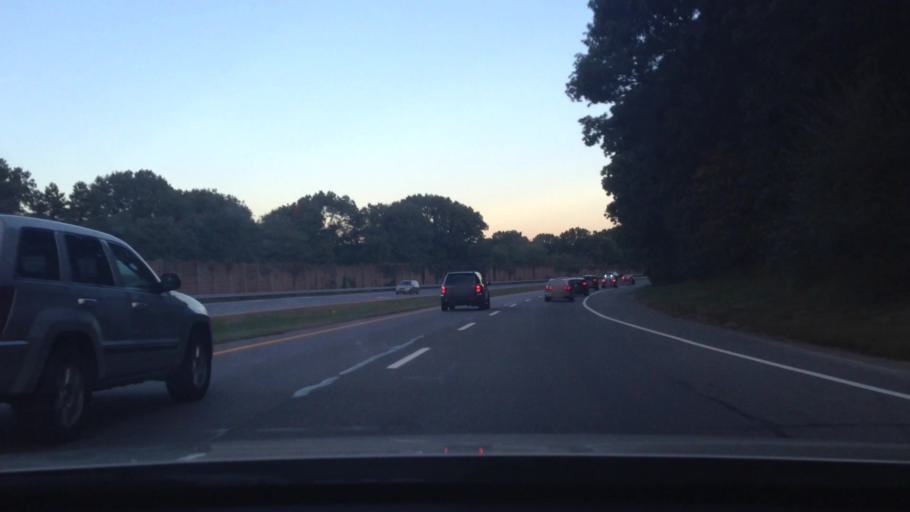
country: US
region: New York
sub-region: Suffolk County
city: Selden
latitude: 40.8512
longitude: -73.0652
